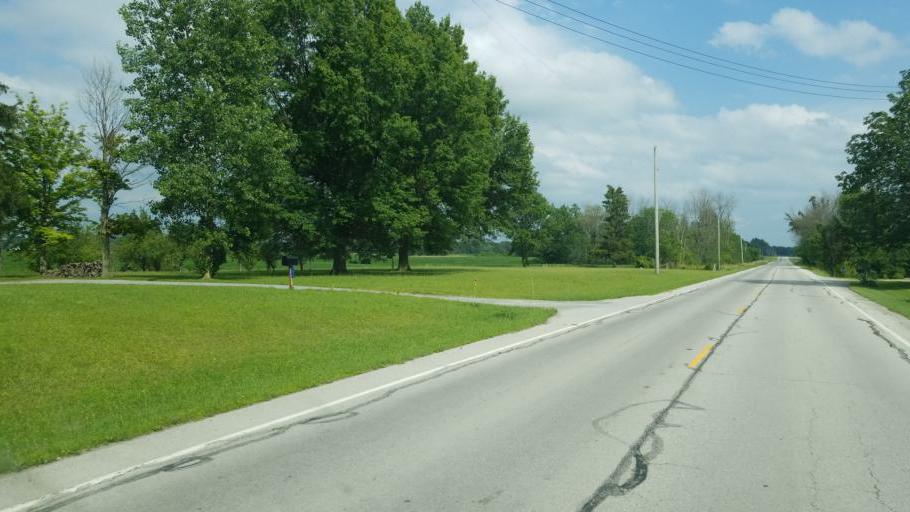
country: US
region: Ohio
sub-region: Crawford County
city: Crestline
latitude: 40.8041
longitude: -82.7710
